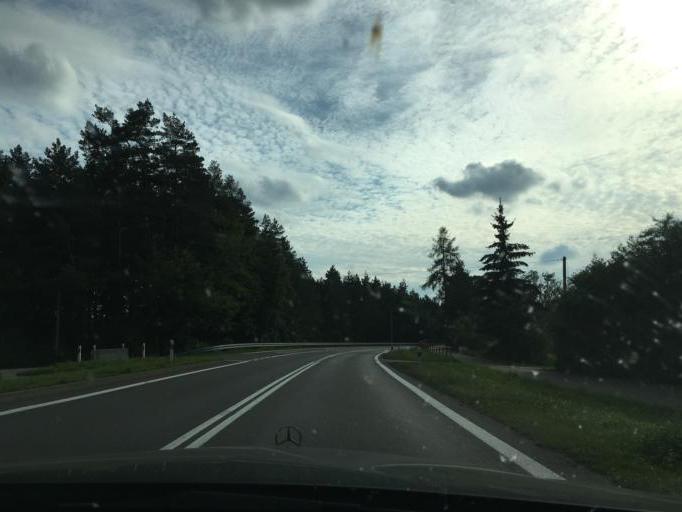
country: PL
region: Podlasie
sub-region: Powiat grajewski
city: Rajgrod
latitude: 53.7089
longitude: 22.6706
